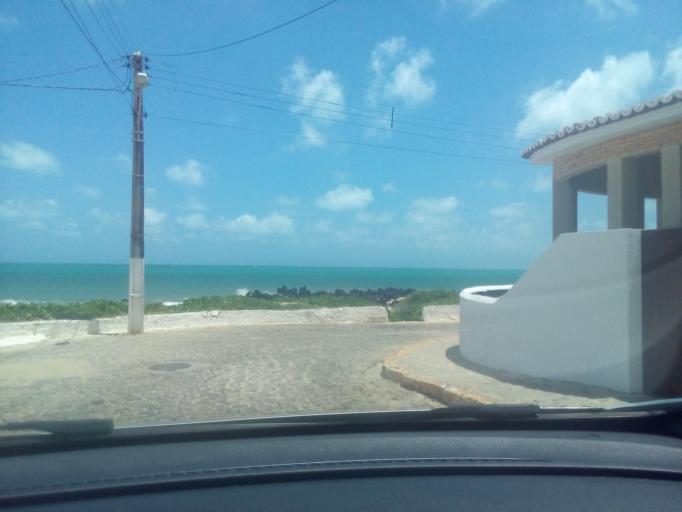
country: BR
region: Rio Grande do Norte
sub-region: Parnamirim
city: Parnamirim
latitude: -5.9677
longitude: -35.1301
